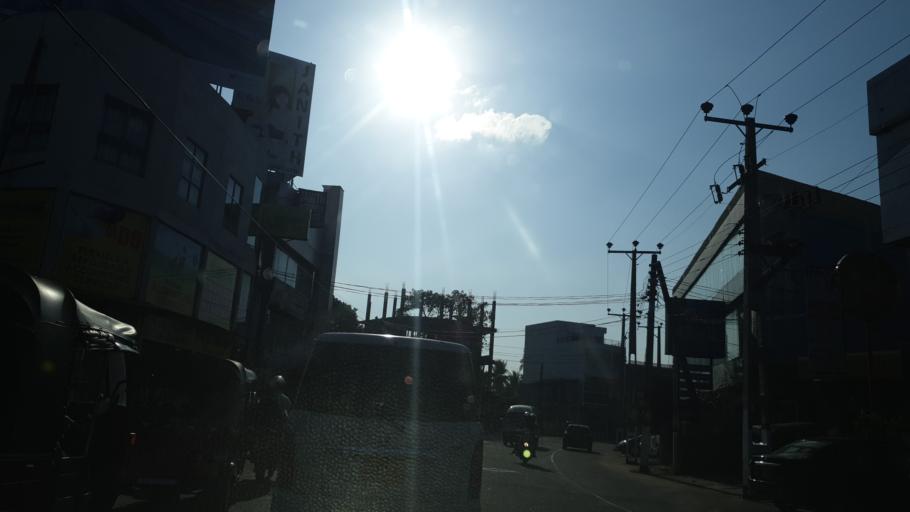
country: LK
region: Western
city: Battaramulla South
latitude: 6.8749
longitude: 79.9339
